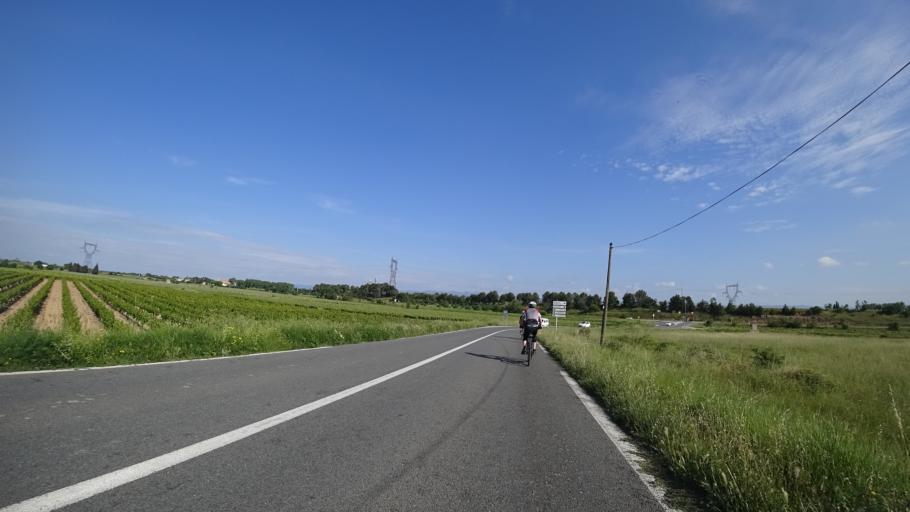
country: FR
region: Languedoc-Roussillon
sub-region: Departement de l'Herault
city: Olonzac
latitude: 43.2642
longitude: 2.7359
